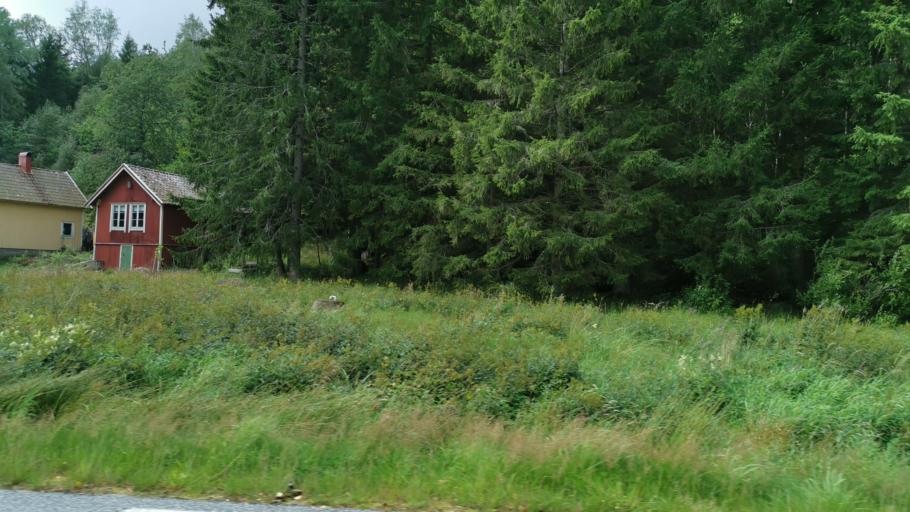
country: SE
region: Vaestra Goetaland
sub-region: Lysekils Kommun
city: Brastad
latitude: 58.4703
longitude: 11.4249
